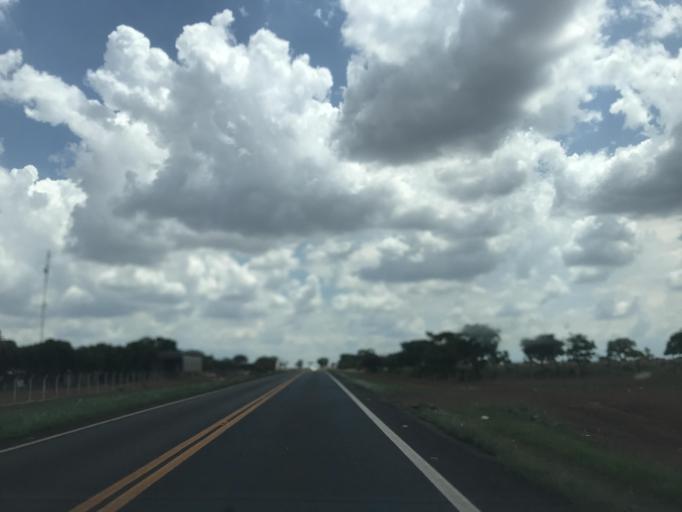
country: BR
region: Goias
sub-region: Piracanjuba
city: Piracanjuba
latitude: -17.4043
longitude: -48.8063
